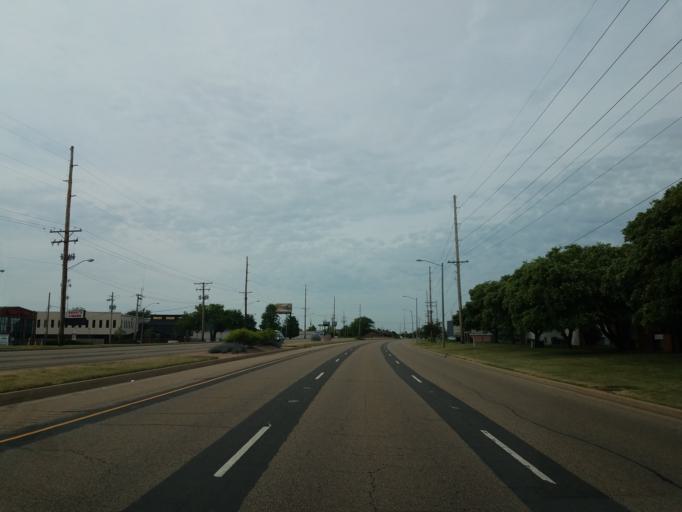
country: US
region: Illinois
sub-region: McLean County
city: Bloomington
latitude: 40.4706
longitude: -88.9530
